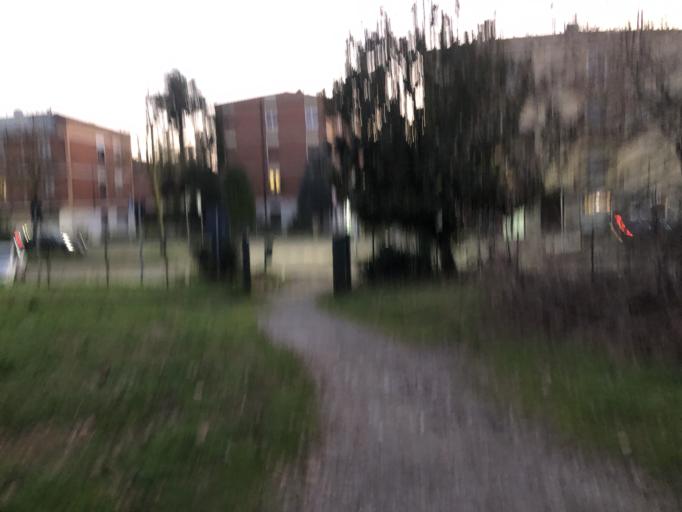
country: IT
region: Emilia-Romagna
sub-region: Provincia di Modena
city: Modena
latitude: 44.6469
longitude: 10.9037
